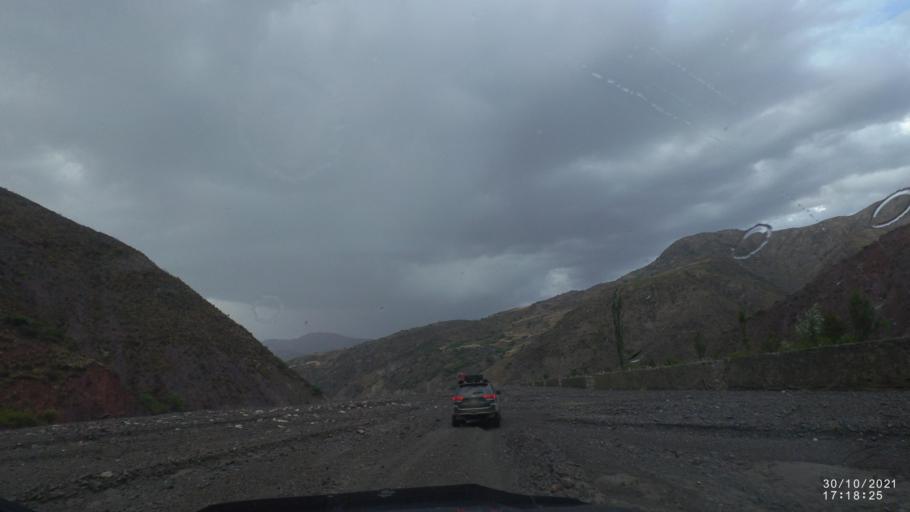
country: BO
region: Cochabamba
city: Colchani
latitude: -17.5361
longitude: -66.6230
